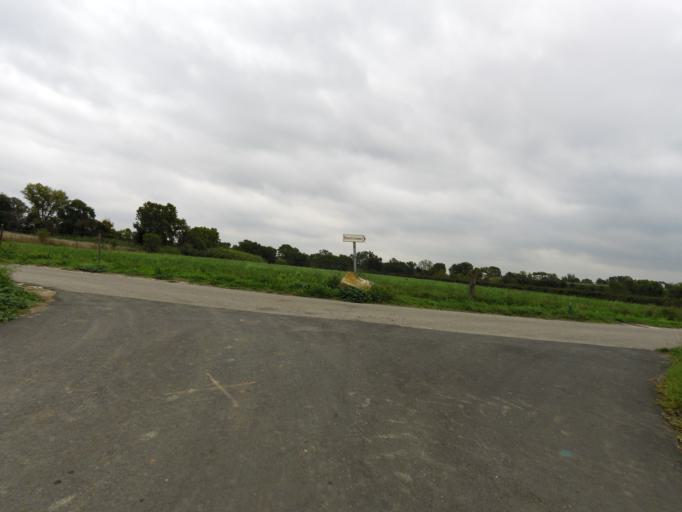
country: FR
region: Languedoc-Roussillon
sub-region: Departement de l'Herault
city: Villetelle
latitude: 43.7234
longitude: 4.1462
